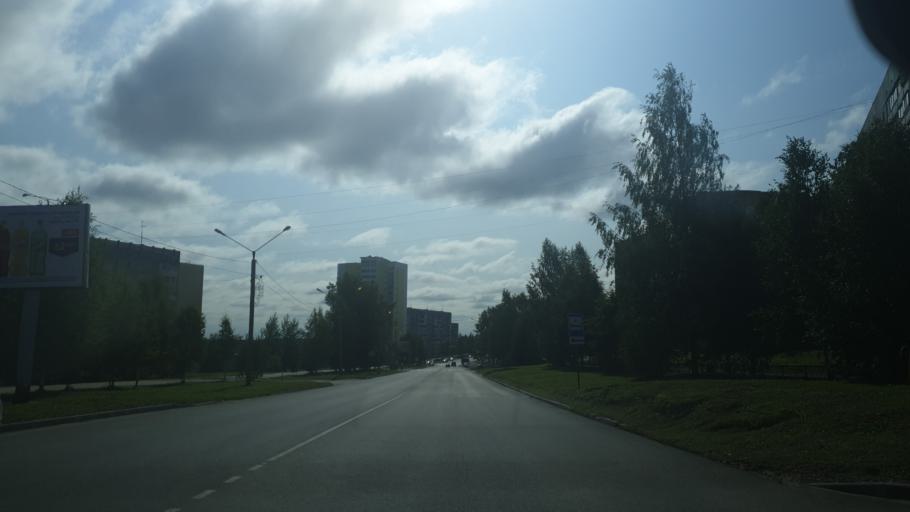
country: RU
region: Komi Republic
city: Ezhva
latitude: 61.7874
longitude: 50.7536
